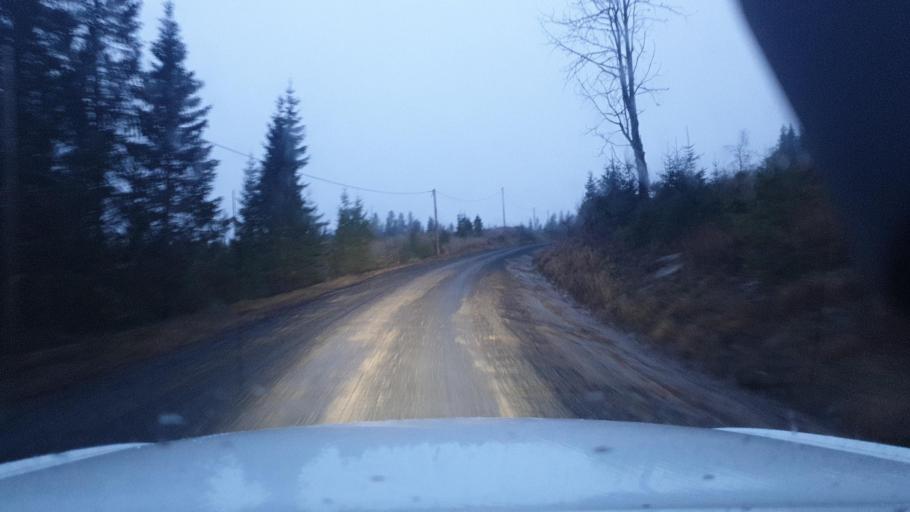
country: SE
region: Vaermland
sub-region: Torsby Kommun
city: Torsby
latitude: 60.1626
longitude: 12.6131
